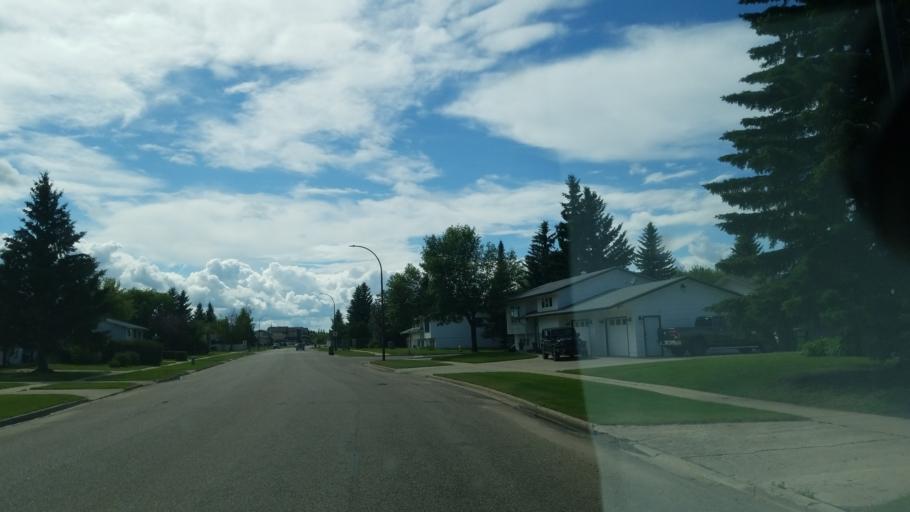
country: CA
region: Saskatchewan
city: Lloydminster
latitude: 53.2670
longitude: -110.0158
